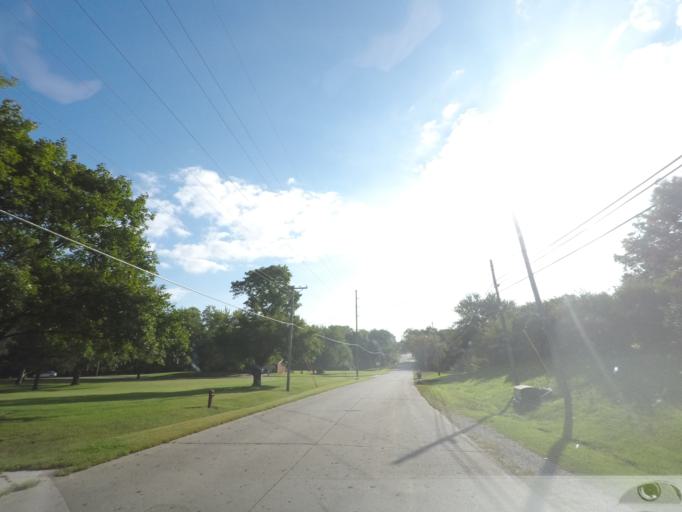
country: US
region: Iowa
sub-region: Story County
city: Nevada
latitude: 42.0156
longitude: -93.4587
